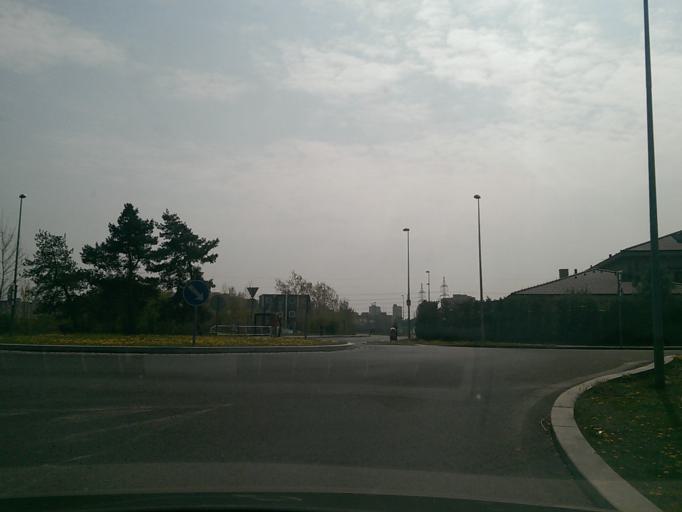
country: CZ
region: Central Bohemia
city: Vestec
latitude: 50.0418
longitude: 14.4996
